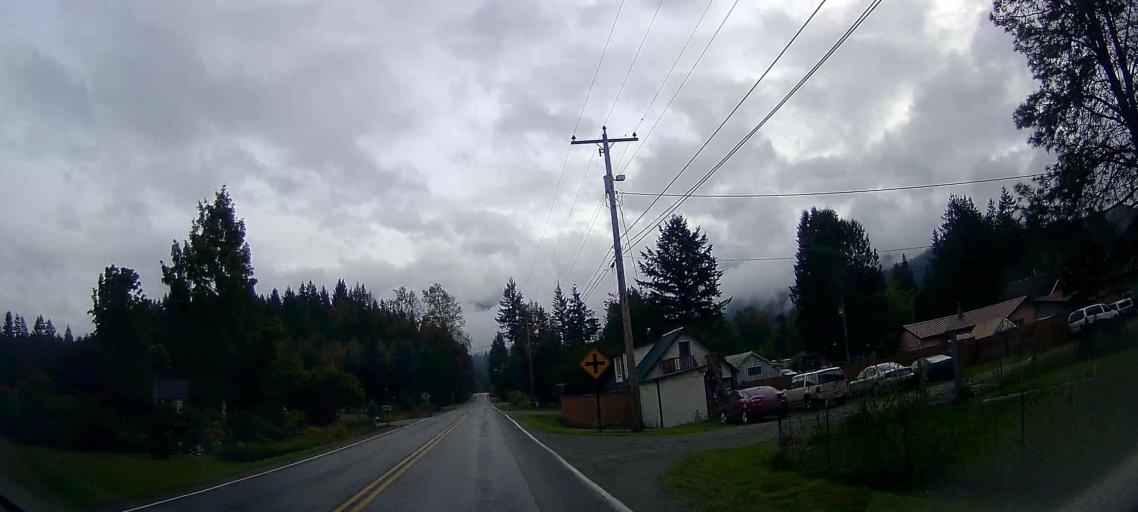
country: US
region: Washington
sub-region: Snohomish County
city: Darrington
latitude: 48.5361
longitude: -121.7661
